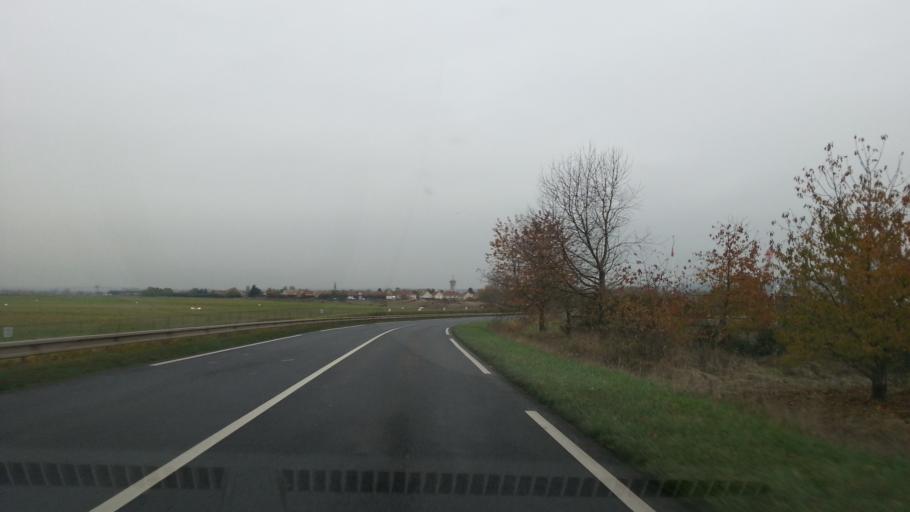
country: FR
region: Ile-de-France
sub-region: Departement du Val-d'Oise
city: Bernes-sur-Oise
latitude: 49.1611
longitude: 2.3102
